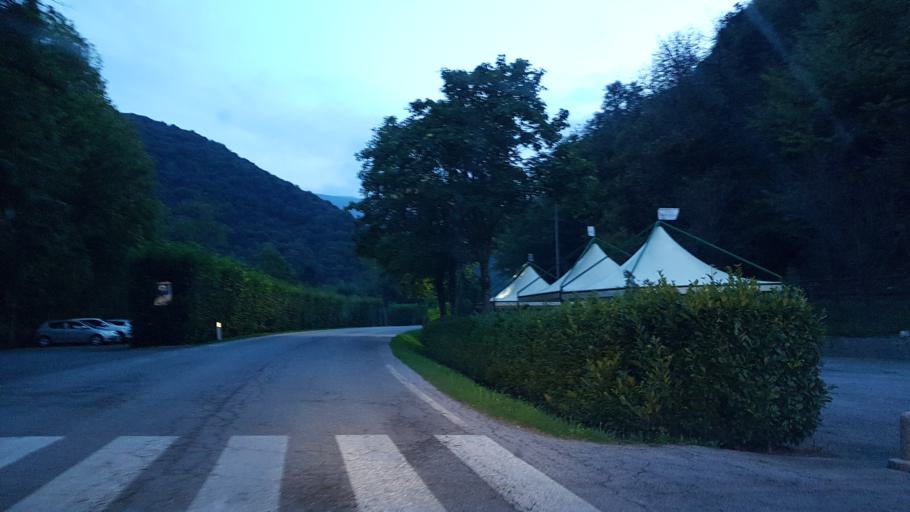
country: IT
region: Piedmont
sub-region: Provincia di Cuneo
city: Roccaforte Mondovi
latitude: 44.2904
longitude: 7.7476
